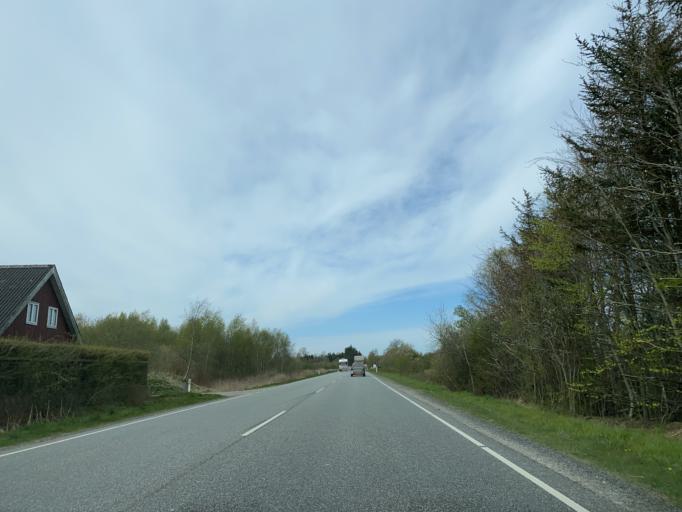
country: DK
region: Central Jutland
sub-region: Favrskov Kommune
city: Hammel
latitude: 56.2626
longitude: 9.7453
